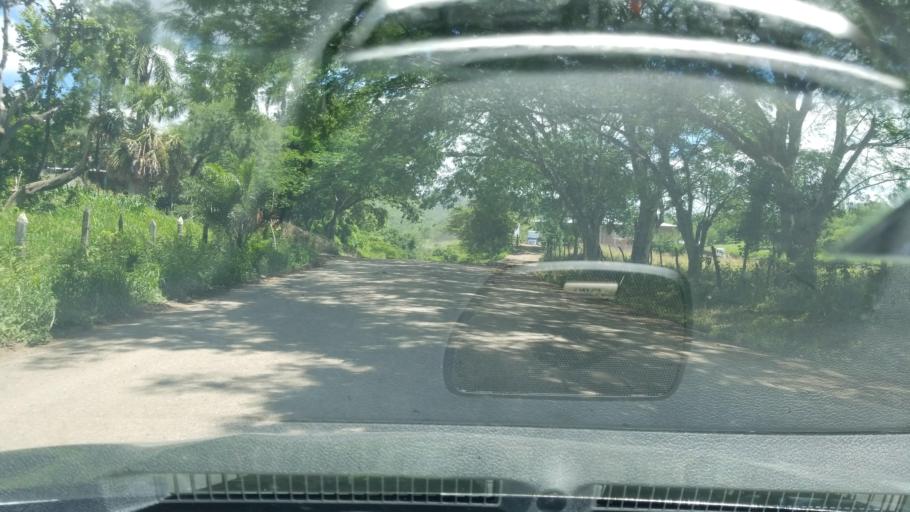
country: HN
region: Francisco Morazan
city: San Juan de Flores
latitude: 14.3130
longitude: -87.0379
